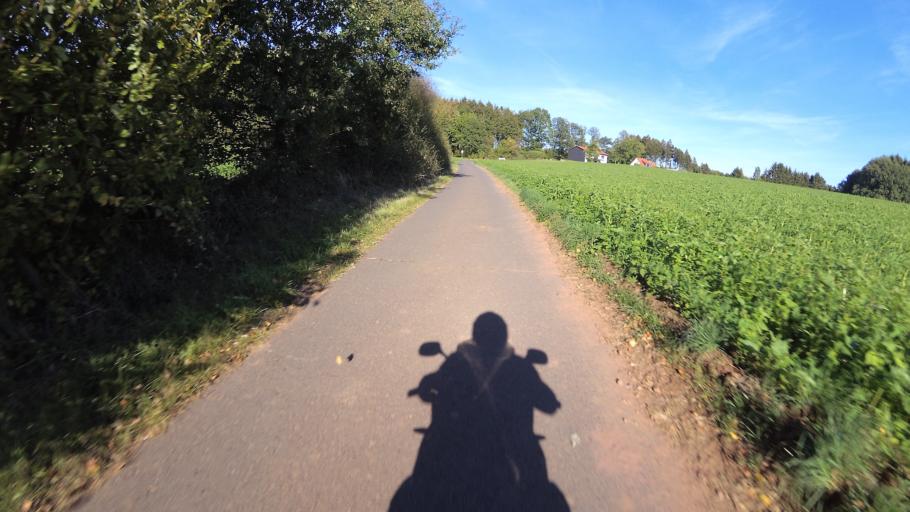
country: DE
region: Saarland
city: Eppelborn
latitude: 49.3581
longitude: 6.9923
